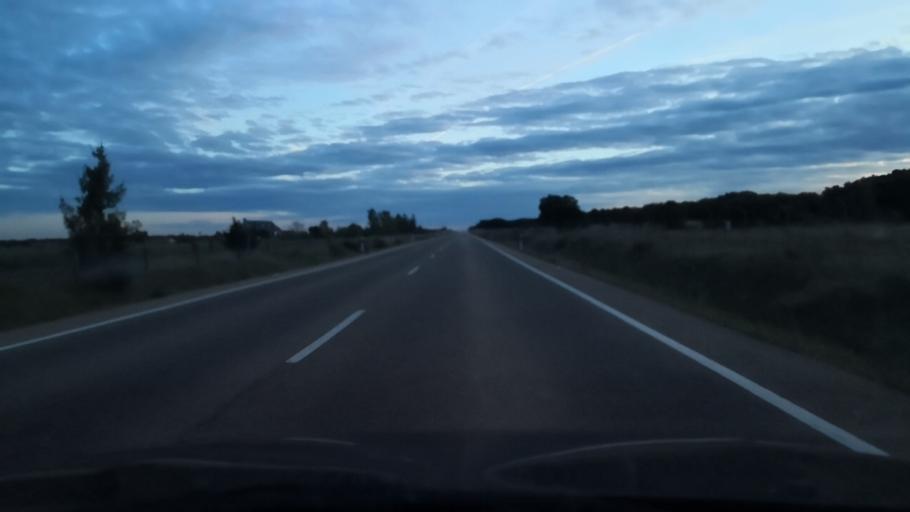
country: ES
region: Extremadura
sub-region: Provincia de Badajoz
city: Villar del Rey
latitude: 39.0096
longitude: -6.8572
